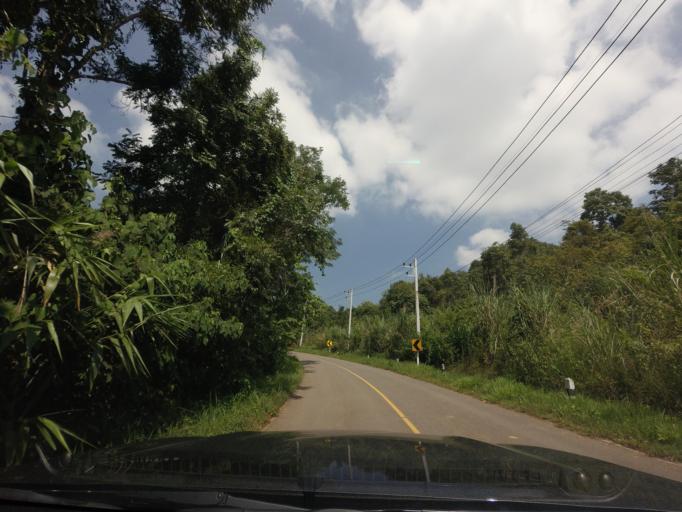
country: TH
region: Loei
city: Na Haeo
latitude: 17.4751
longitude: 100.9190
